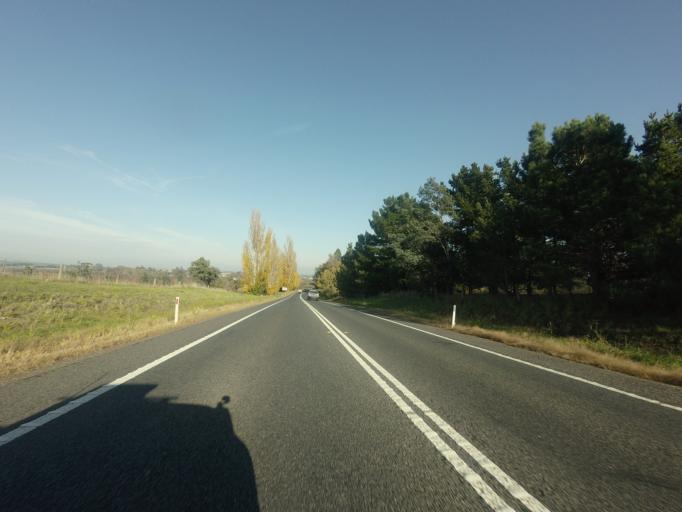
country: AU
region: Tasmania
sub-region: Northern Midlands
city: Longford
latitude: -41.5830
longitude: 147.1315
